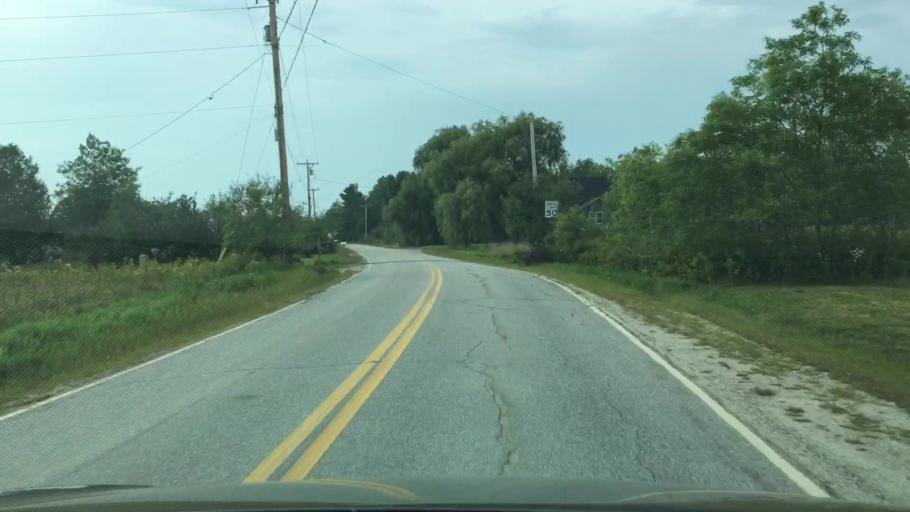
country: US
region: Maine
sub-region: Hancock County
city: Penobscot
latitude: 44.4690
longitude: -68.7405
